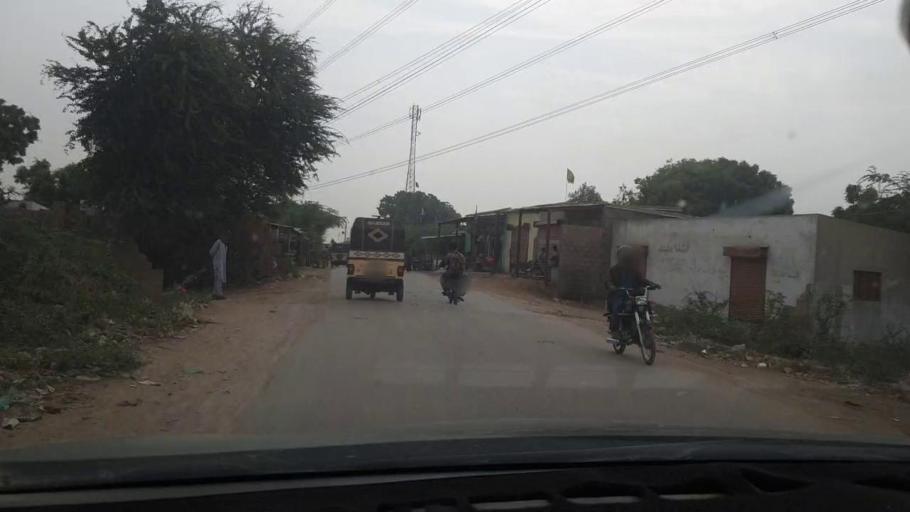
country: PK
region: Sindh
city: Malir Cantonment
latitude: 24.9079
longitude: 67.2857
